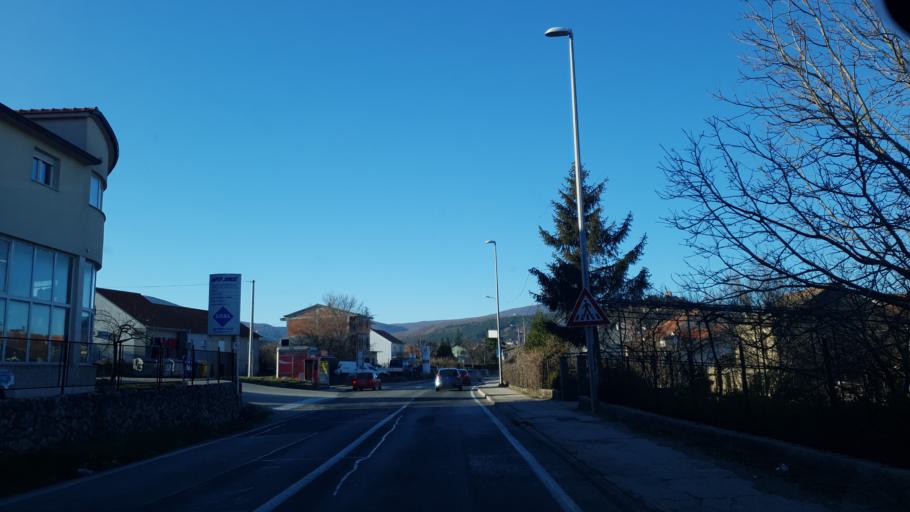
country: HR
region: Splitsko-Dalmatinska
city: Sinj
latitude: 43.6930
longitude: 16.6434
